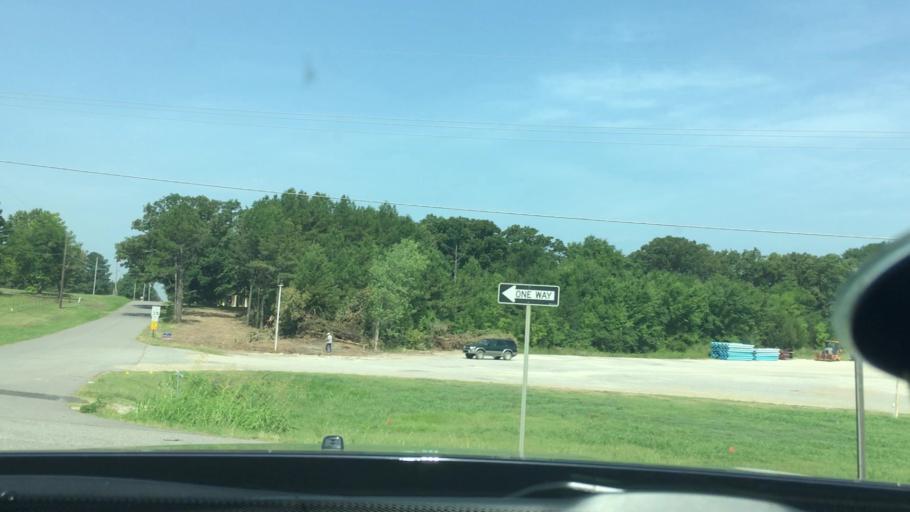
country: US
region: Oklahoma
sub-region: Atoka County
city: Atoka
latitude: 34.3603
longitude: -96.1447
